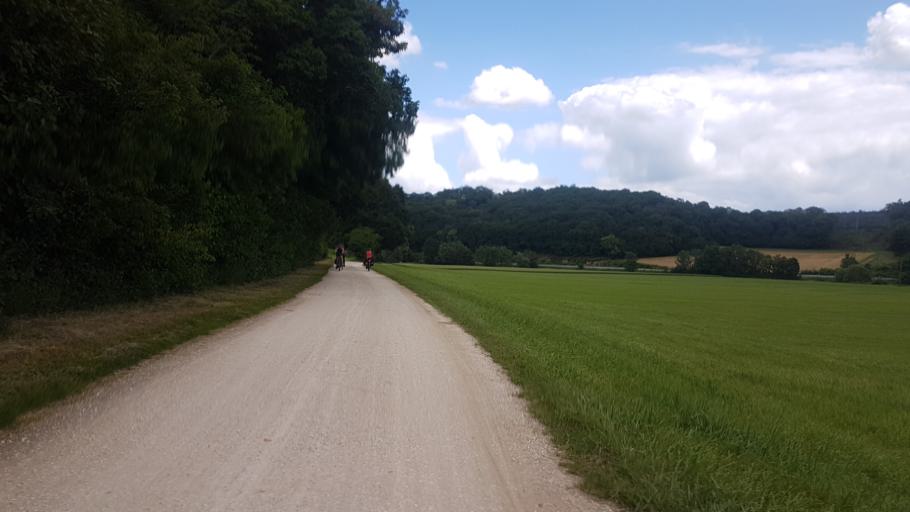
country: DE
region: Bavaria
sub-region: Regierungsbezirk Mittelfranken
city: Solnhofen
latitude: 48.8795
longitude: 11.0277
